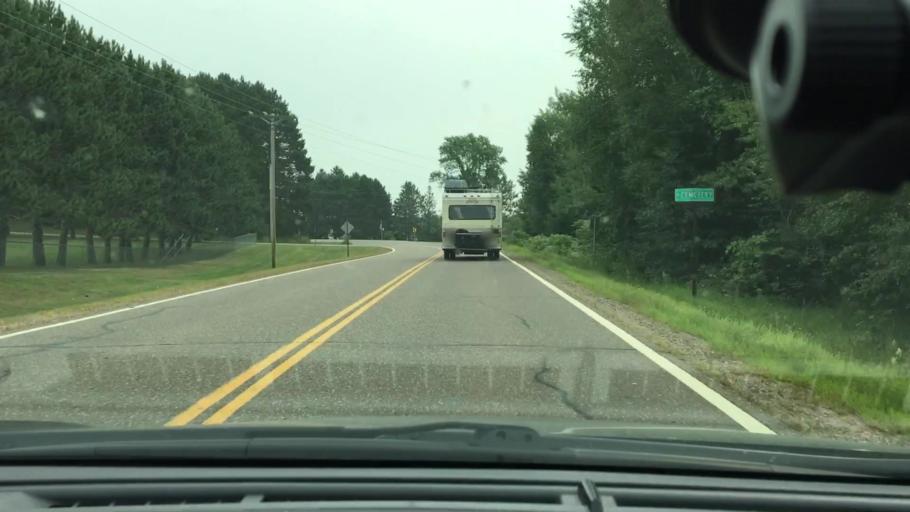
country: US
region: Minnesota
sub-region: Aitkin County
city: Aitkin
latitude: 46.4010
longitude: -93.7714
